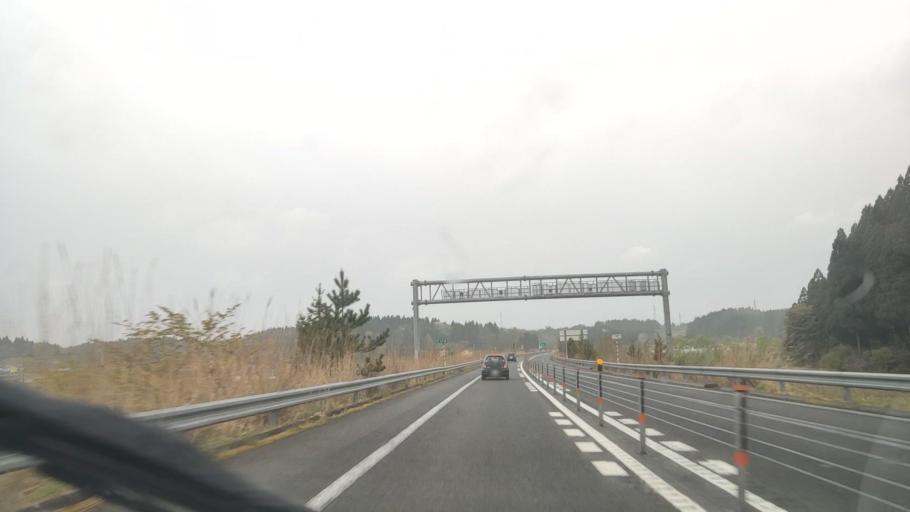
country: JP
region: Akita
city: Noshiromachi
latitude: 40.1878
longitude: 140.1004
